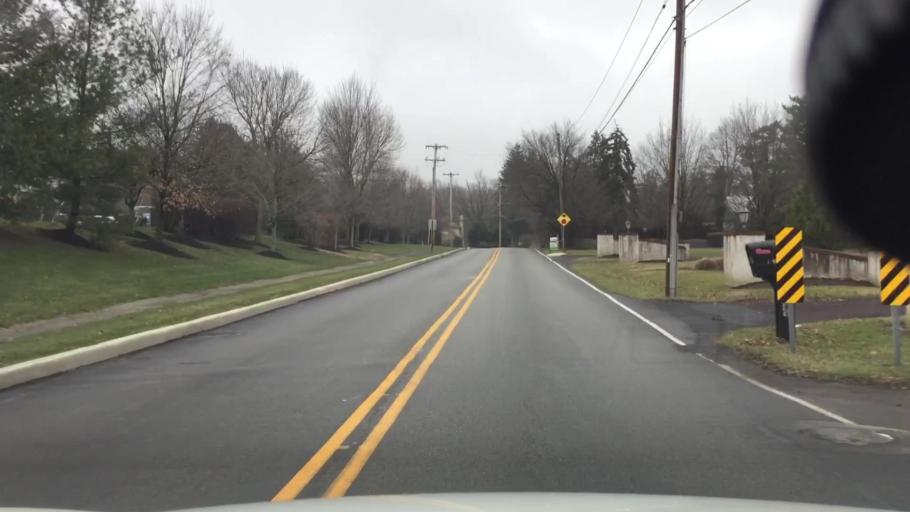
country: US
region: Pennsylvania
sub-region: Montgomery County
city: Dresher
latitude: 40.1549
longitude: -75.1787
